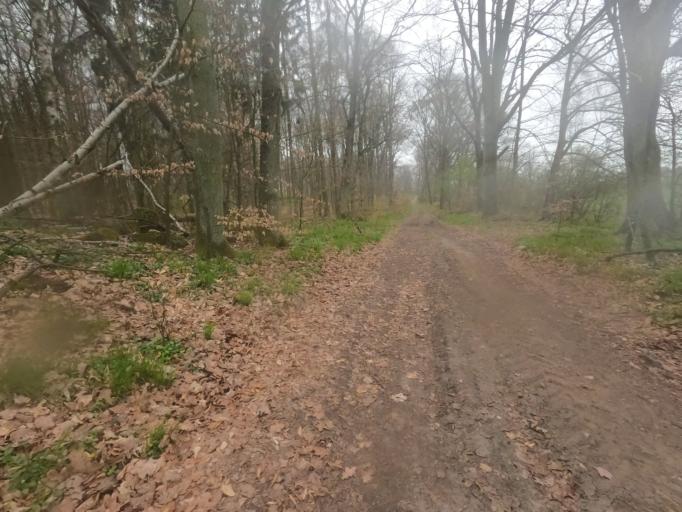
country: PL
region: West Pomeranian Voivodeship
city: Trzcinsko Zdroj
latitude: 52.9253
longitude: 14.7179
